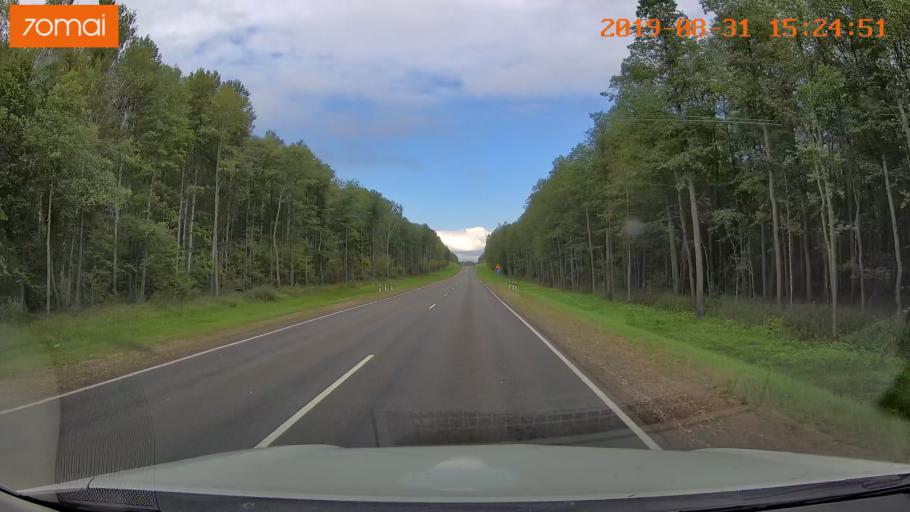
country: RU
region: Kaluga
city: Baryatino
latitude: 54.5333
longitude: 34.5108
